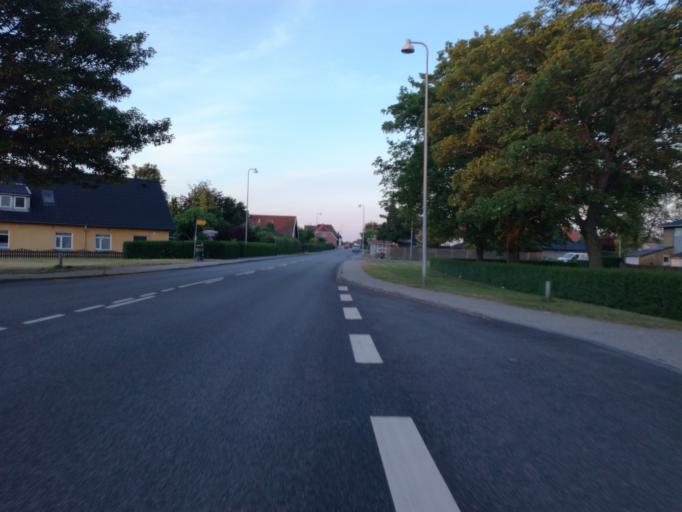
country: DK
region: South Denmark
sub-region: Fredericia Kommune
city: Fredericia
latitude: 55.5777
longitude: 9.7536
